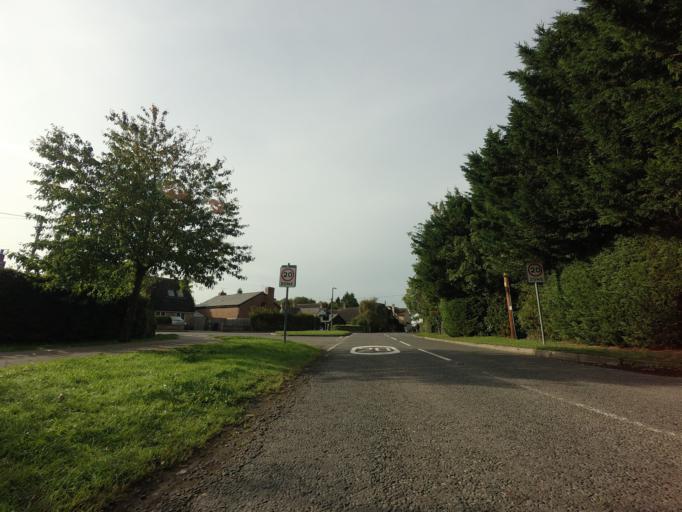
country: GB
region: England
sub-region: Cambridgeshire
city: Harston
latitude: 52.0946
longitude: 0.0784
